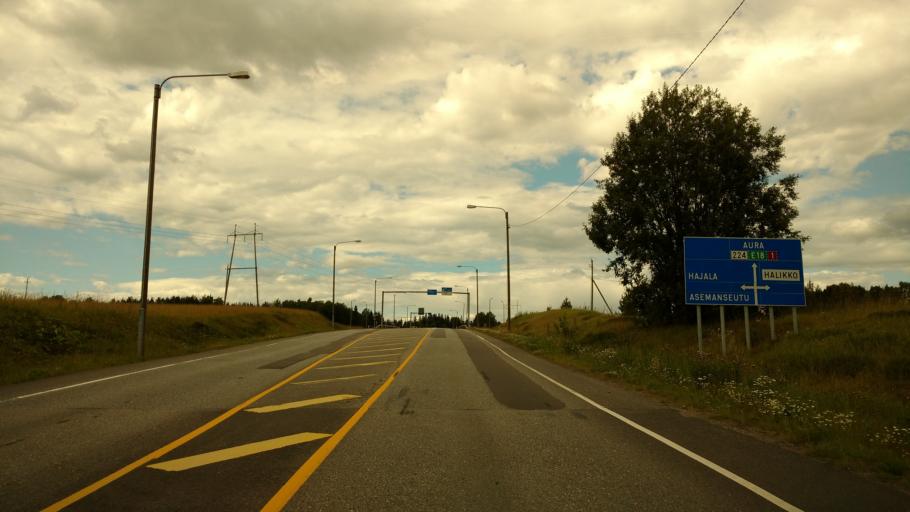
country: FI
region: Varsinais-Suomi
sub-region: Salo
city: Halikko
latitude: 60.3977
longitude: 23.0529
